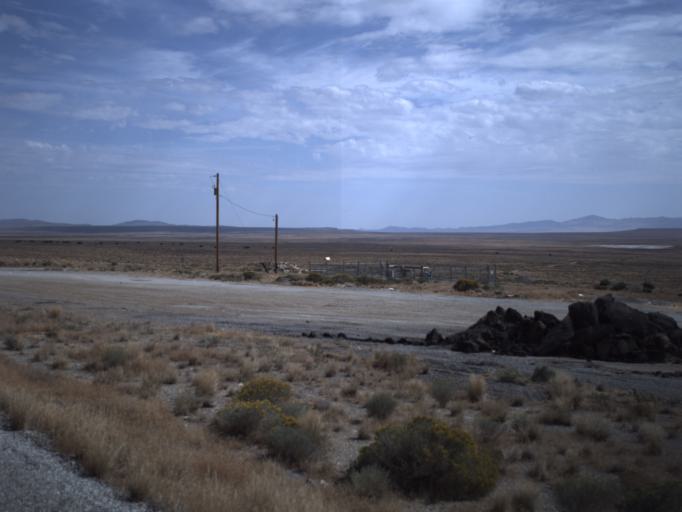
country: US
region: Utah
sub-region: Tooele County
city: Wendover
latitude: 41.4961
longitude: -113.6128
